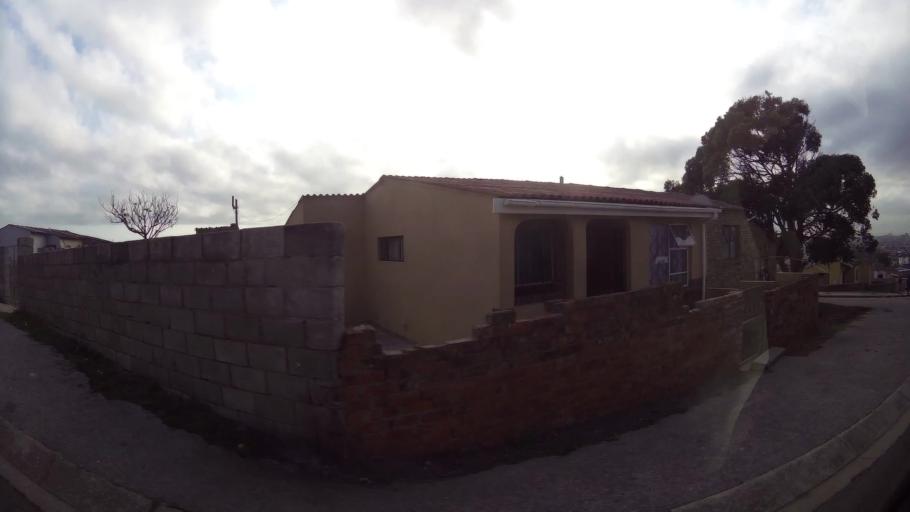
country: ZA
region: Eastern Cape
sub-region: Nelson Mandela Bay Metropolitan Municipality
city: Port Elizabeth
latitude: -33.9194
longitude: 25.5451
